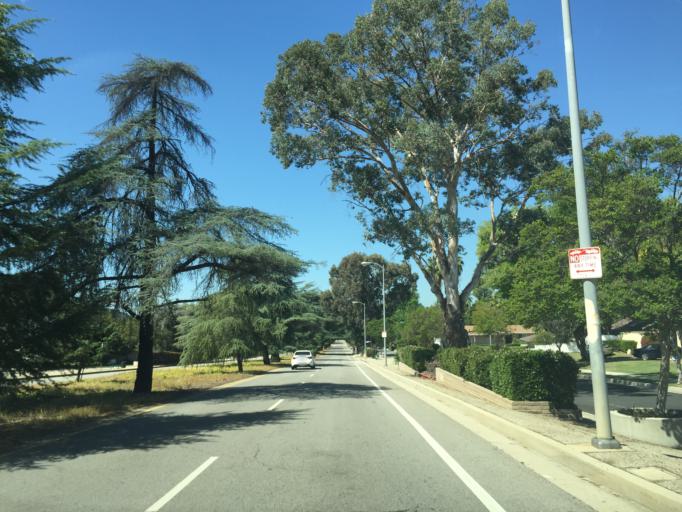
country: US
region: California
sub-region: Los Angeles County
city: Calabasas
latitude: 34.1507
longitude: -118.6238
